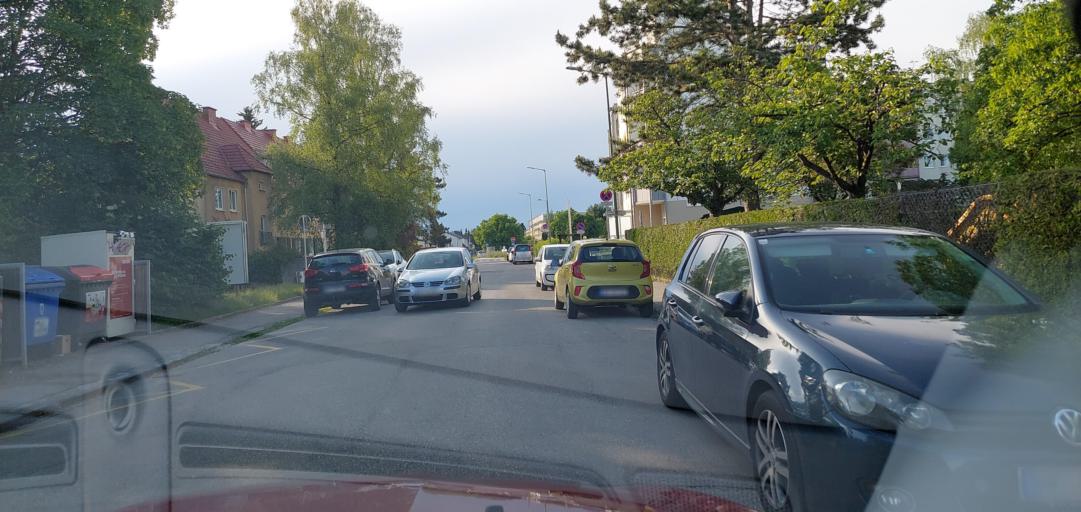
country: AT
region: Upper Austria
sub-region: Wels Stadt
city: Wels
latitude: 48.1625
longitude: 14.0056
